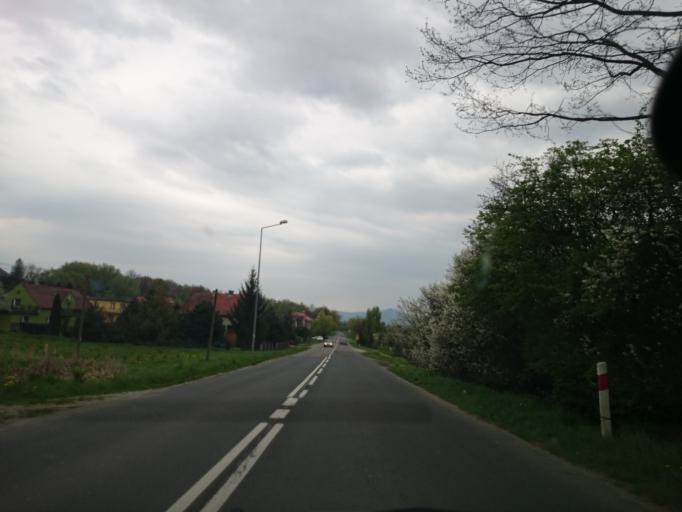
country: PL
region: Opole Voivodeship
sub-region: Powiat nyski
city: Glucholazy
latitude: 50.3744
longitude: 17.3597
